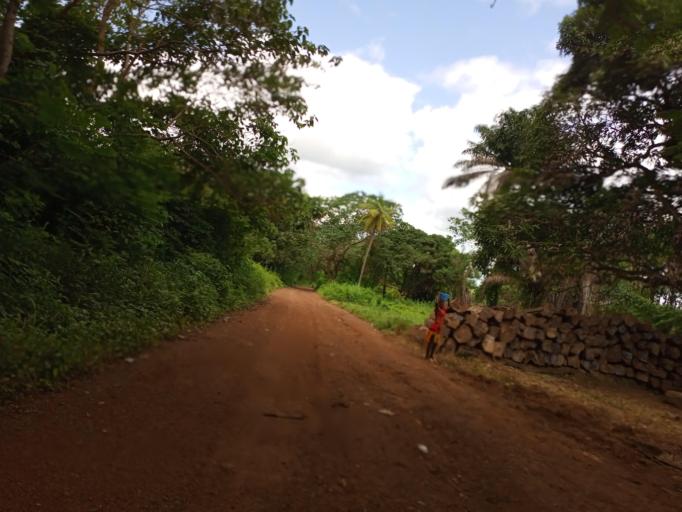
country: SL
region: Northern Province
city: Kamakwie
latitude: 9.5081
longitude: -12.2230
